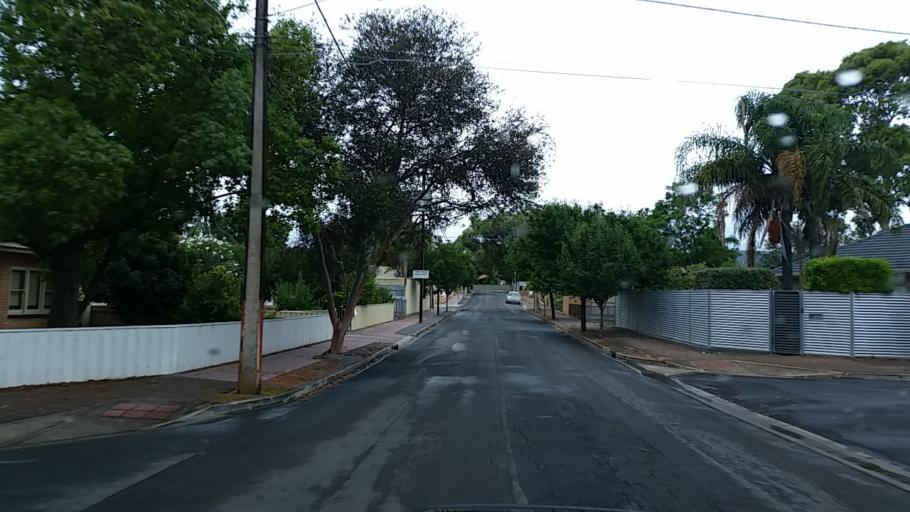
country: AU
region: South Australia
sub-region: Norwood Payneham St Peters
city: Payneham
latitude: -34.9000
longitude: 138.6463
